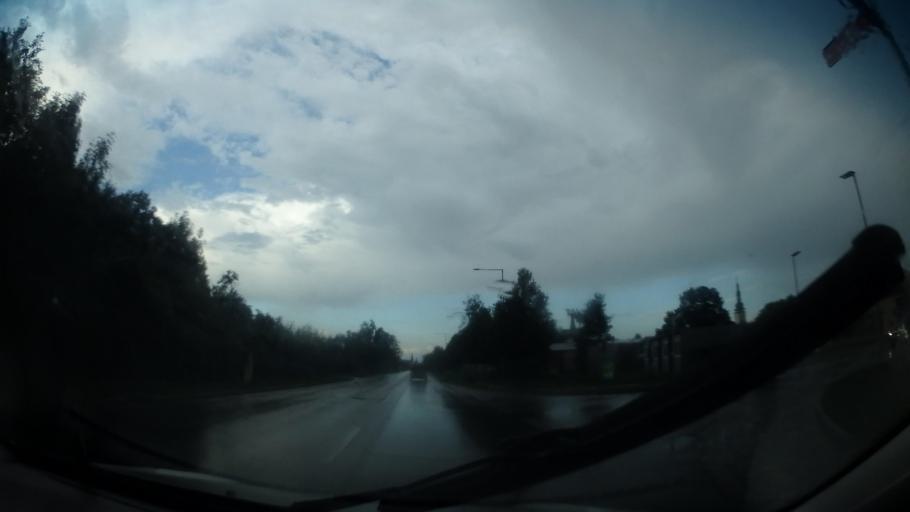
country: CZ
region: Olomoucky
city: Litovel
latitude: 49.6995
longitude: 17.0709
